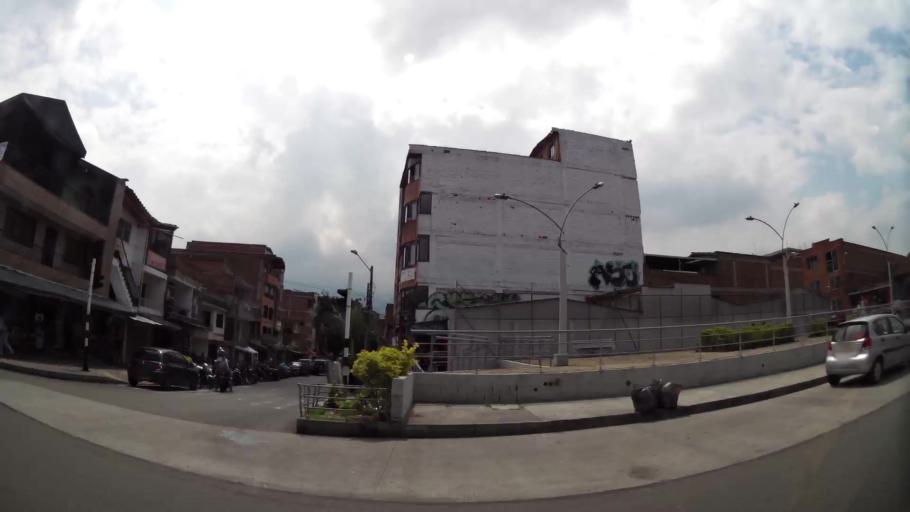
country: CO
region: Antioquia
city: Itagui
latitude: 6.1894
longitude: -75.5952
